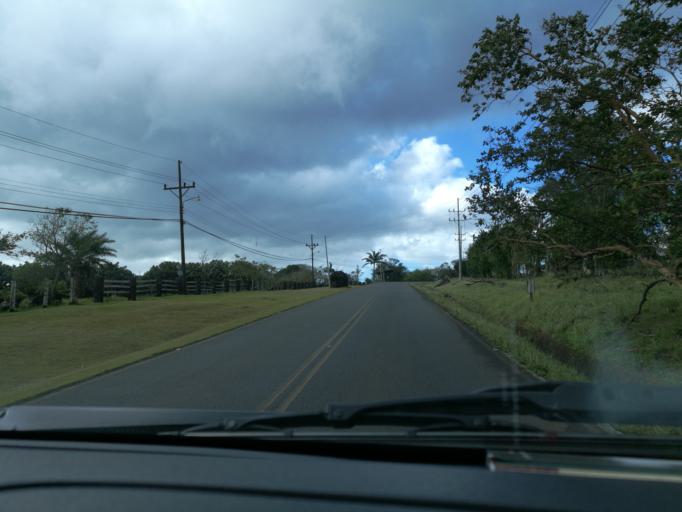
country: CR
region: Alajuela
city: Bijagua
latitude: 10.6850
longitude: -85.0873
